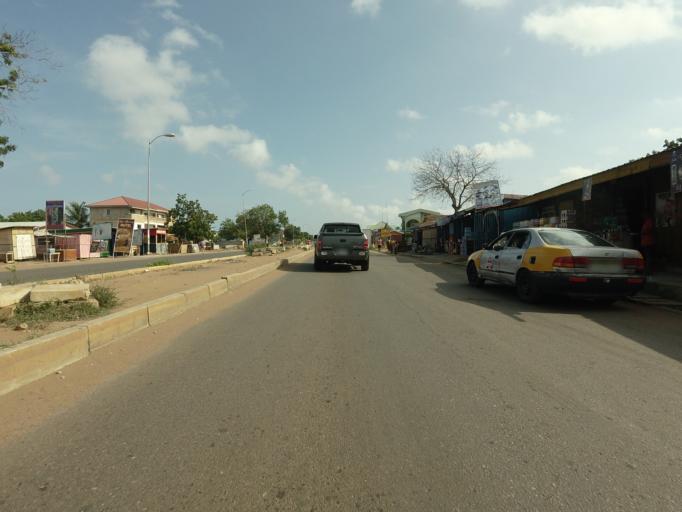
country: GH
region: Greater Accra
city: Tema
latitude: 5.6643
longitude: -0.0497
